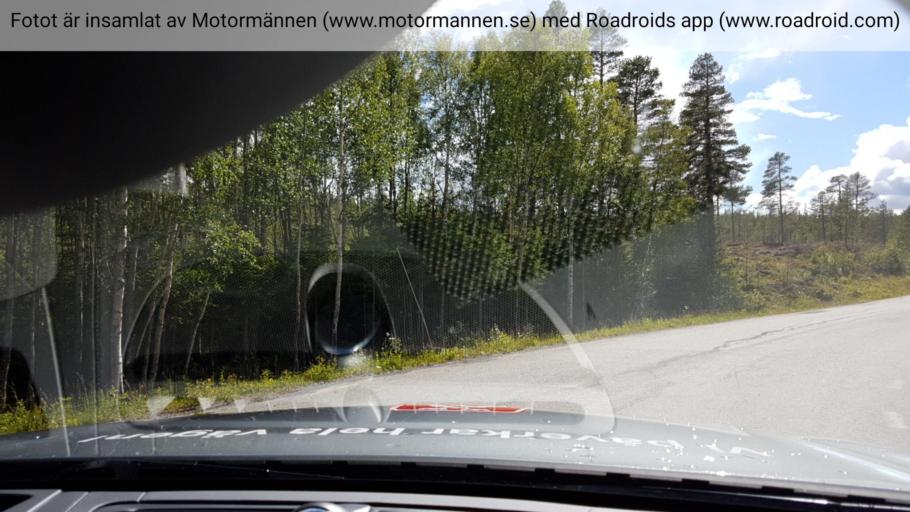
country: SE
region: Jaemtland
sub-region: Bergs Kommun
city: Hoverberg
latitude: 63.0283
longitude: 14.0728
